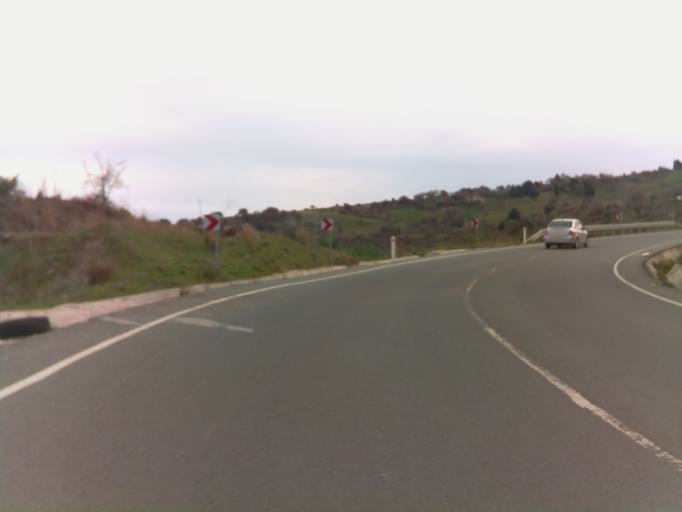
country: CY
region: Pafos
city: Polis
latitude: 34.9742
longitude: 32.4057
